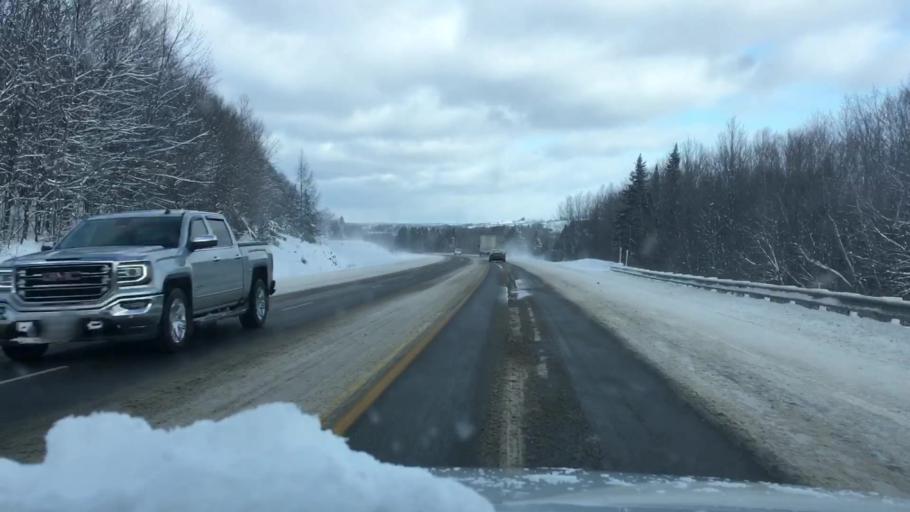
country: US
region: Maine
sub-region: Aroostook County
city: Caribou
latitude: 46.8231
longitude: -67.9935
